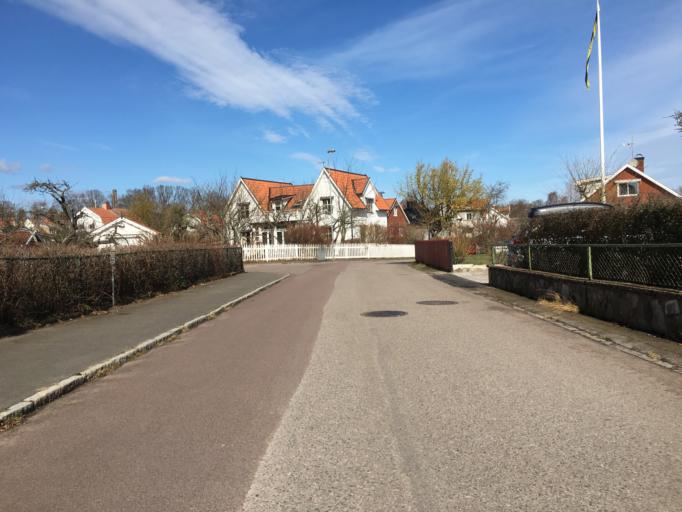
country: SE
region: Kalmar
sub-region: Kalmar Kommun
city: Kalmar
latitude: 56.6525
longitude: 16.3326
